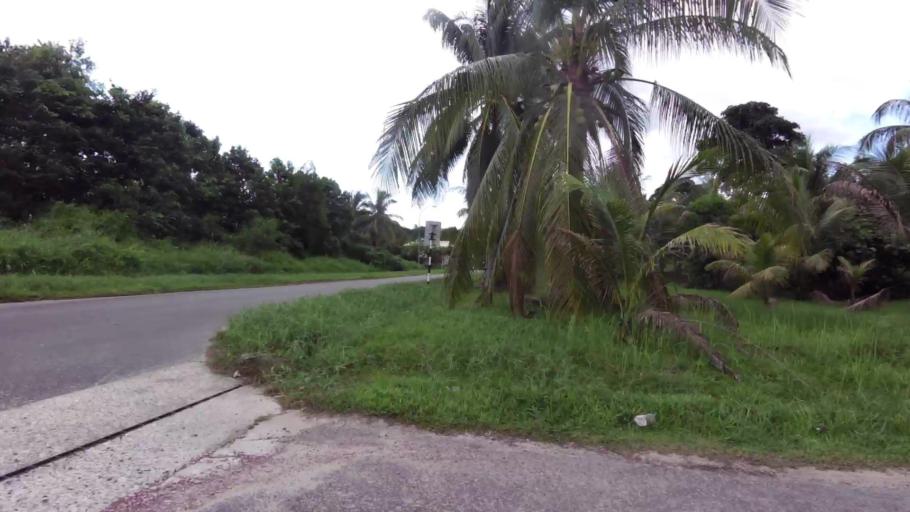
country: BN
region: Brunei and Muara
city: Bandar Seri Begawan
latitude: 4.9487
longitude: 114.9589
